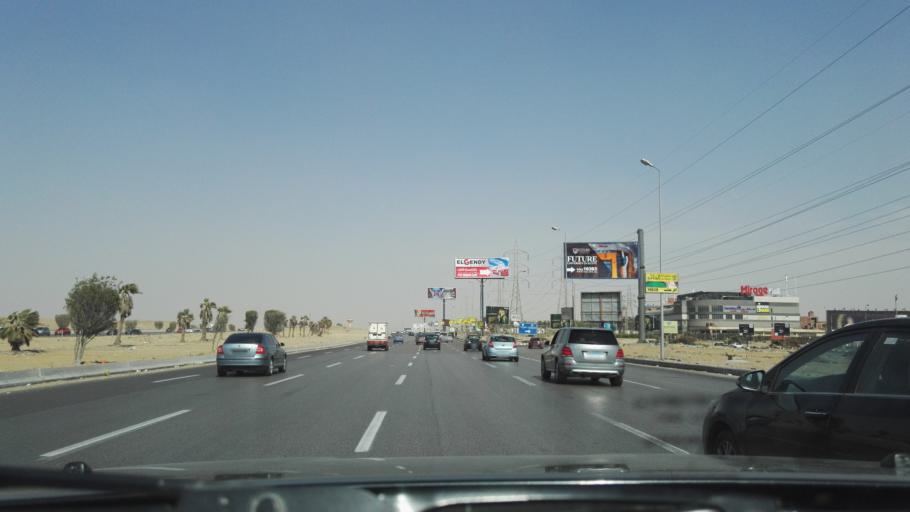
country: EG
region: Muhafazat al Qalyubiyah
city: Al Khankah
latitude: 30.0808
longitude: 31.4496
